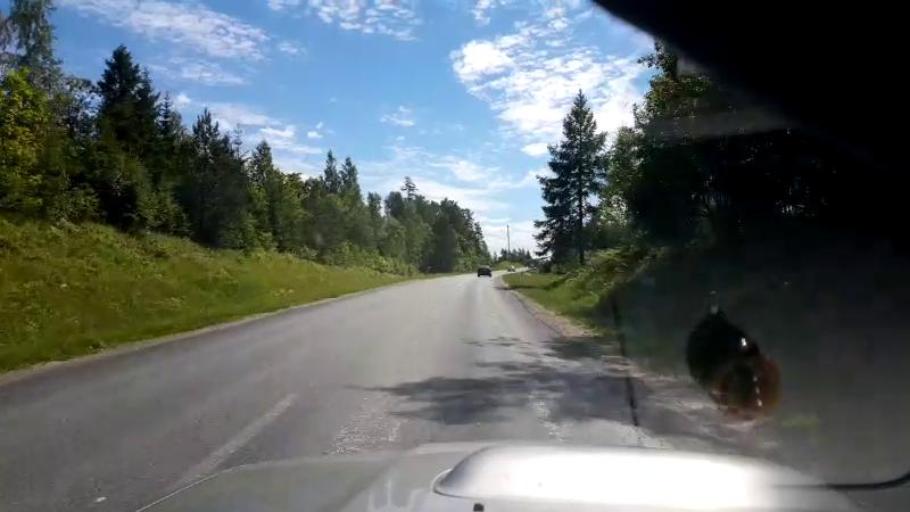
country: EE
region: Jogevamaa
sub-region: Jogeva linn
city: Jogeva
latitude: 58.8410
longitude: 26.2908
